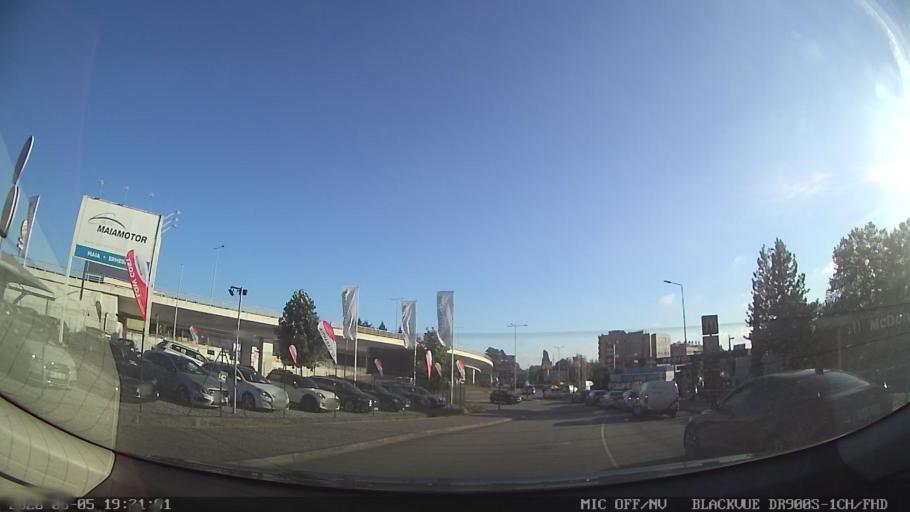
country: PT
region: Porto
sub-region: Gondomar
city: Baguim do Monte
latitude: 41.2056
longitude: -8.5477
